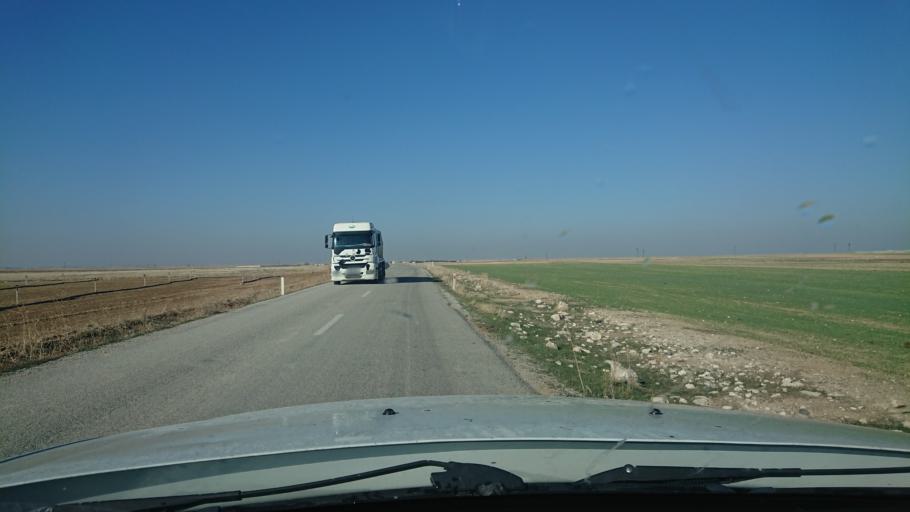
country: TR
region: Aksaray
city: Sultanhani
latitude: 38.2989
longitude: 33.5108
